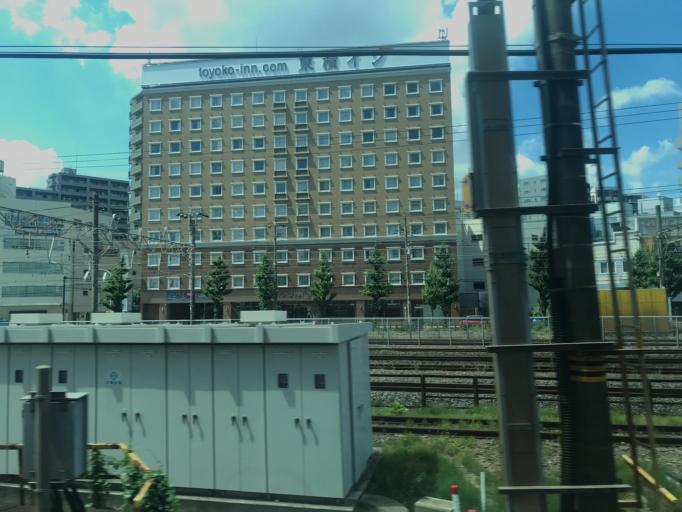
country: JP
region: Kanagawa
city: Fujisawa
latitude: 35.3385
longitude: 139.4836
